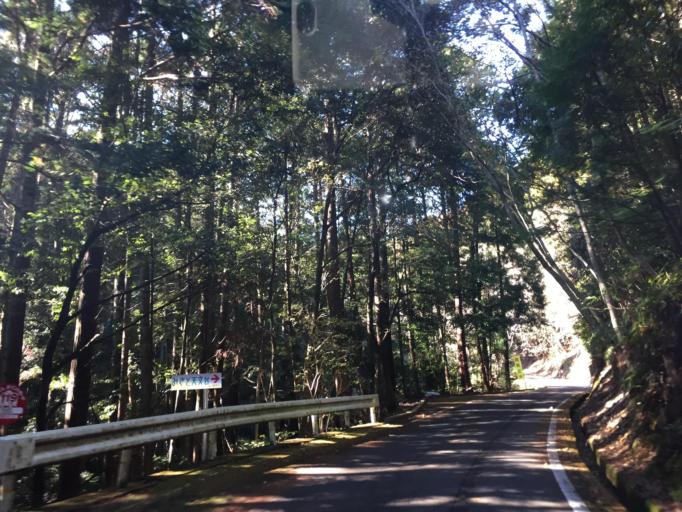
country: JP
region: Wakayama
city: Iwade
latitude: 34.1442
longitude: 135.4128
